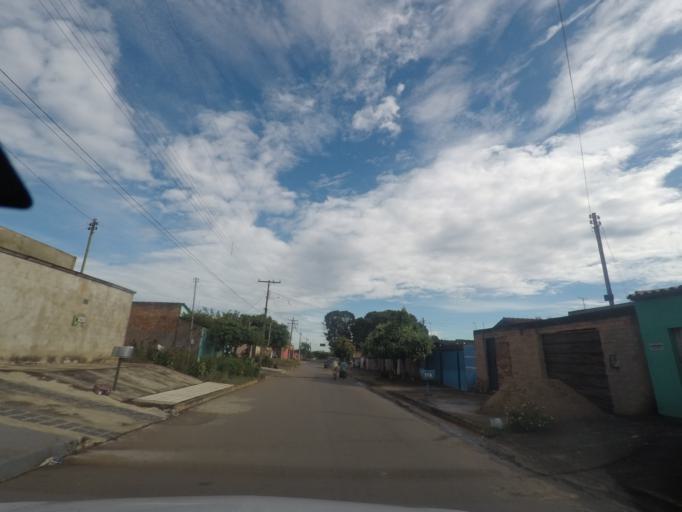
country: BR
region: Goias
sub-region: Aparecida De Goiania
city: Aparecida de Goiania
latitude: -16.8200
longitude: -49.3057
